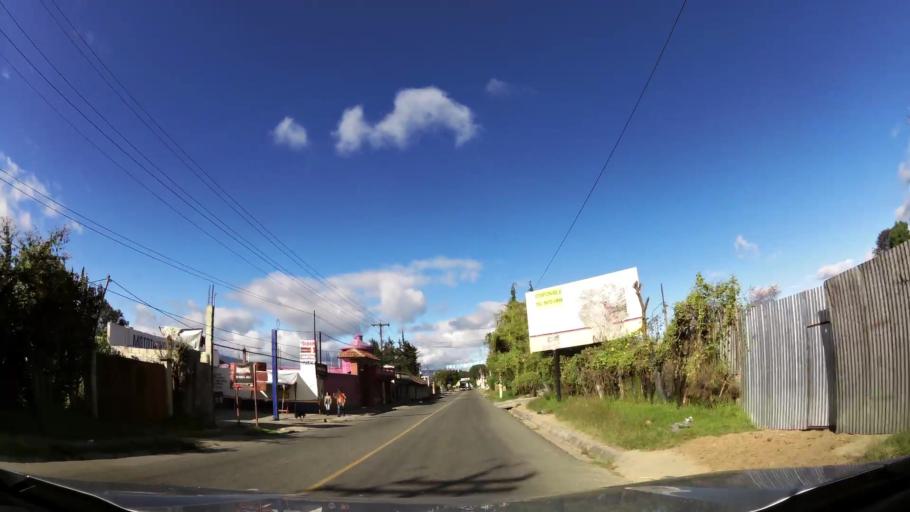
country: GT
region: Quiche
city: Chichicastenango
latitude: 14.9525
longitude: -91.1074
